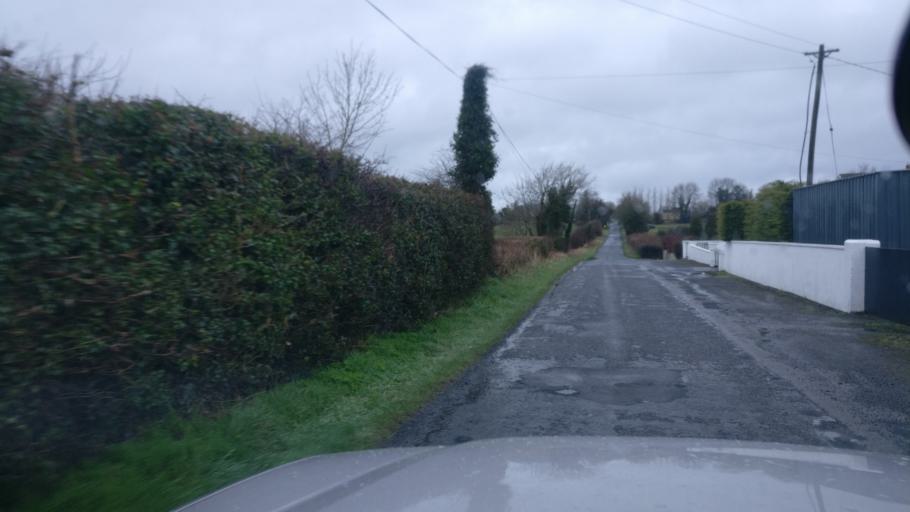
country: IE
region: Connaught
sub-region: County Galway
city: Ballinasloe
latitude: 53.2492
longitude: -8.3568
